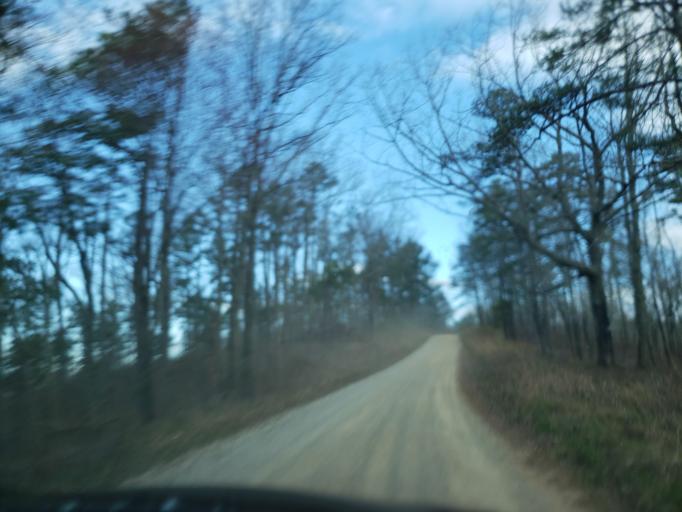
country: US
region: Alabama
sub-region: Cleburne County
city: Heflin
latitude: 33.6687
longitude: -85.6349
